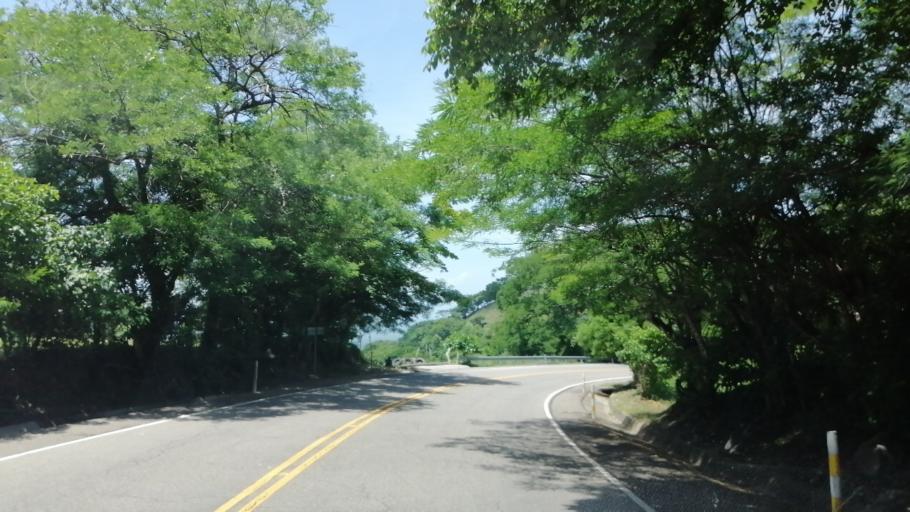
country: SV
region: Chalatenango
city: Nueva Concepcion
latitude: 14.1716
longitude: -89.3107
